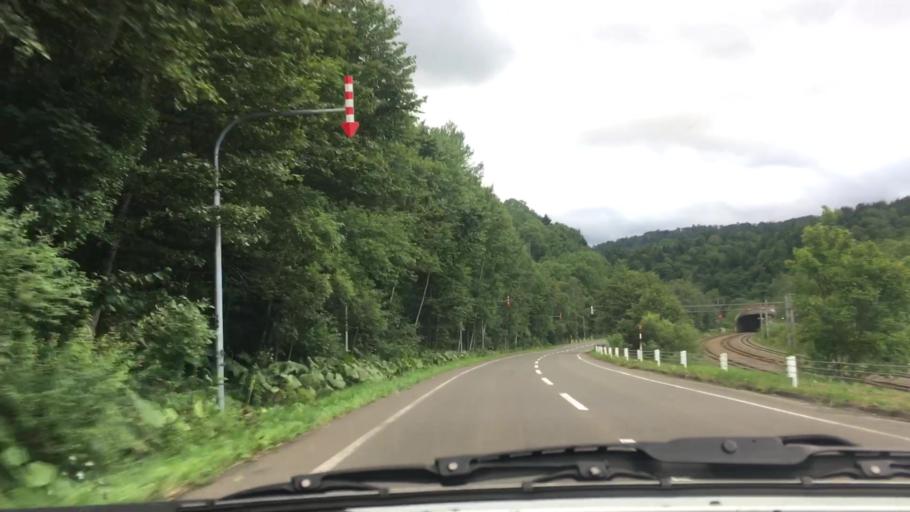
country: JP
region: Hokkaido
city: Shimo-furano
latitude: 43.0745
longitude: 142.6740
